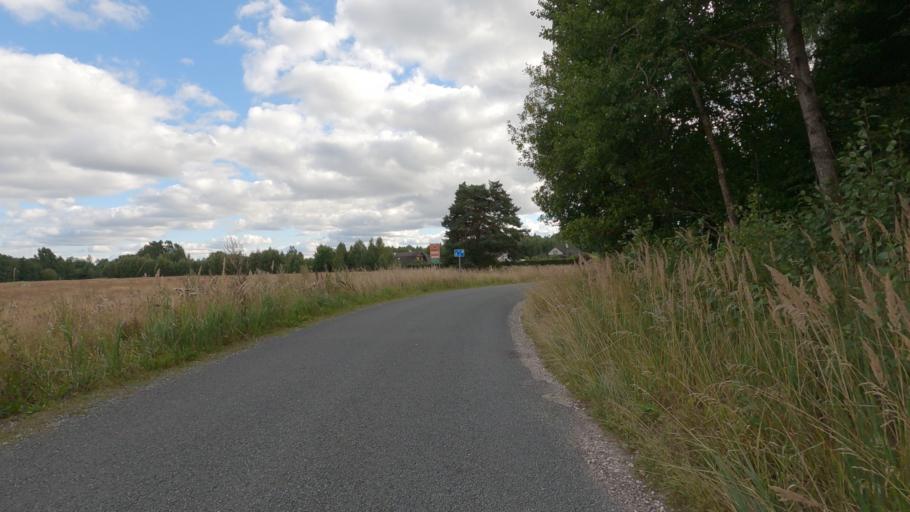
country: EE
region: Raplamaa
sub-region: Rapla vald
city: Rapla
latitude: 59.0080
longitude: 24.7734
